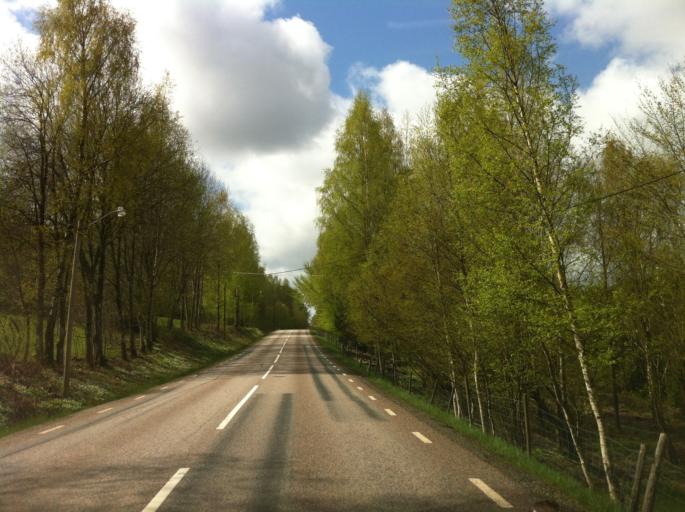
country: SE
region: Vaestra Goetaland
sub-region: Alingsas Kommun
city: Ingared
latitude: 57.8505
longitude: 12.5293
